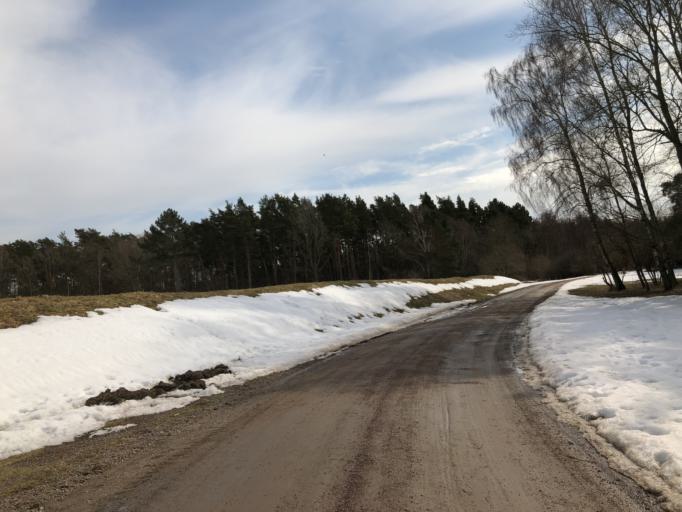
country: SE
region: Kalmar
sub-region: Kalmar Kommun
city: Kalmar
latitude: 56.6604
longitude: 16.3171
